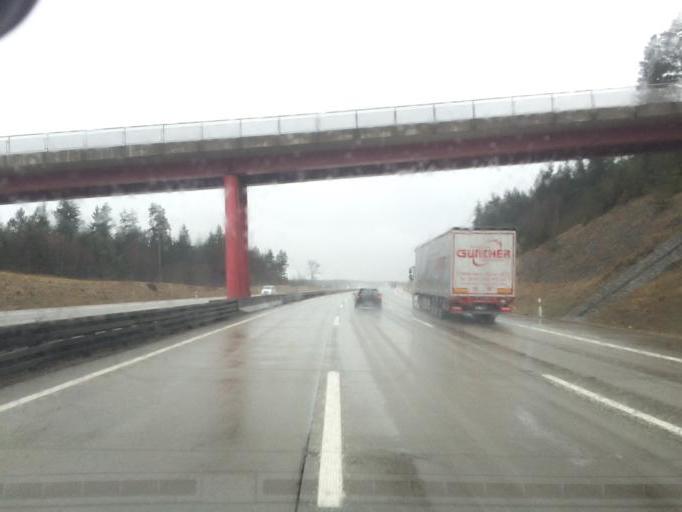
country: DE
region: Thuringia
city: Tanna
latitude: 50.5116
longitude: 11.7973
